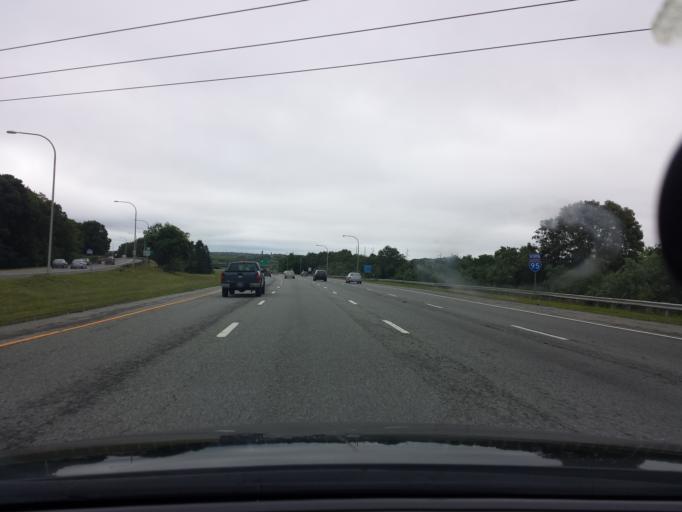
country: US
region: Rhode Island
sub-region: Kent County
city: East Greenwich
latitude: 41.7093
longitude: -71.4716
